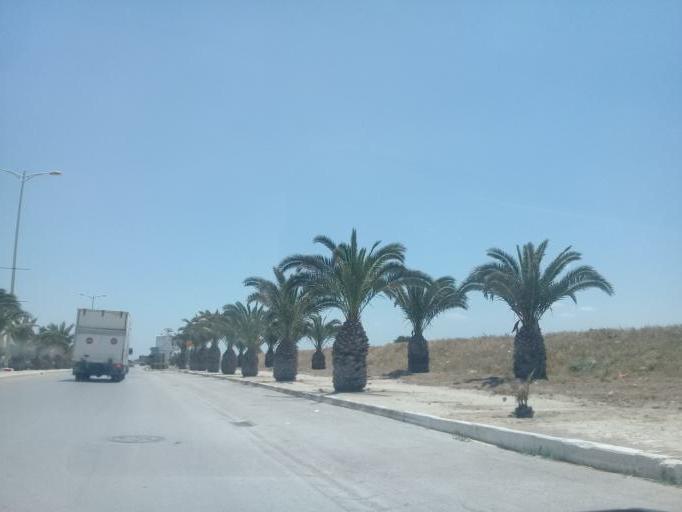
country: TN
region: Tunis
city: La Goulette
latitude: 36.8444
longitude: 10.2622
